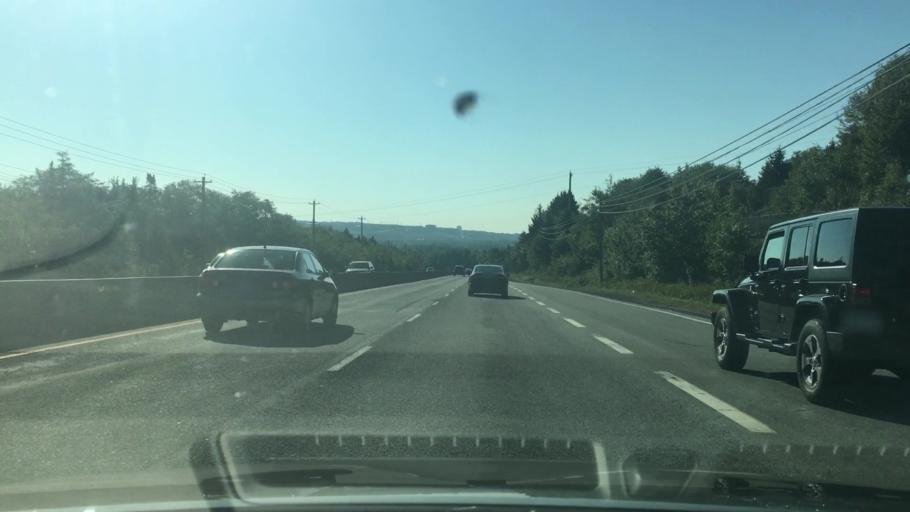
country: CA
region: Nova Scotia
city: Dartmouth
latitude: 44.7120
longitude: -63.6282
